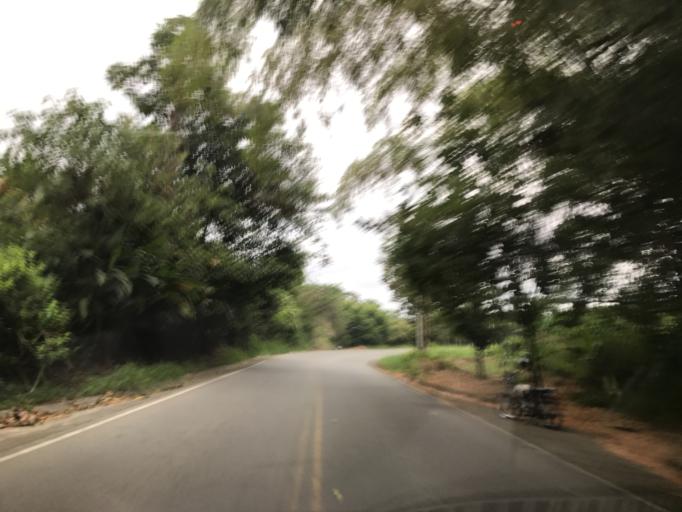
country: CO
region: Quindio
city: Buenavista
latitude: 4.3900
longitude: -75.7559
